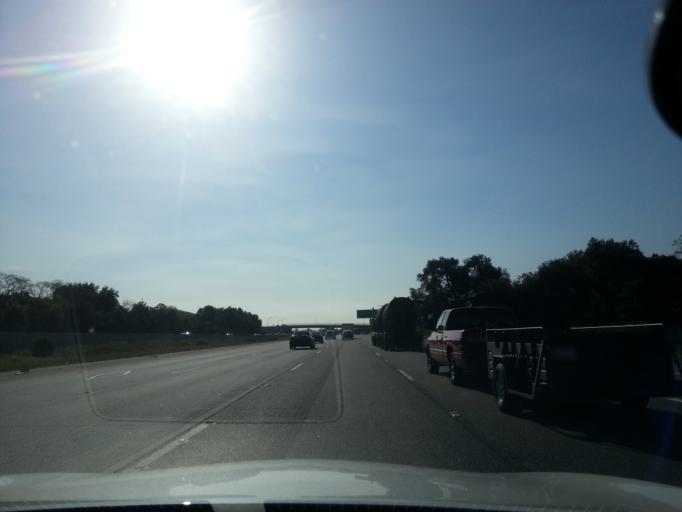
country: US
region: California
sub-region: Santa Clara County
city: Morgan Hill
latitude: 37.2143
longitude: -121.7279
